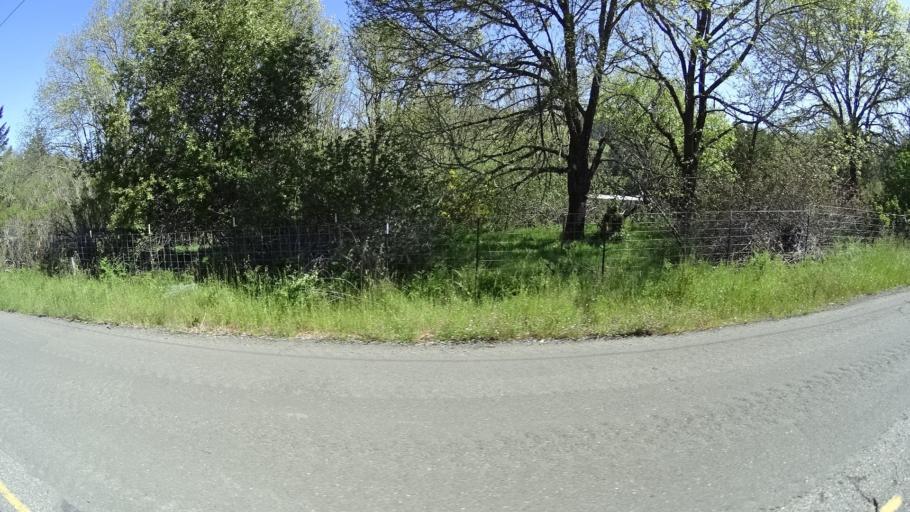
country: US
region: California
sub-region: Humboldt County
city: Rio Dell
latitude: 40.2465
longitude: -124.1647
